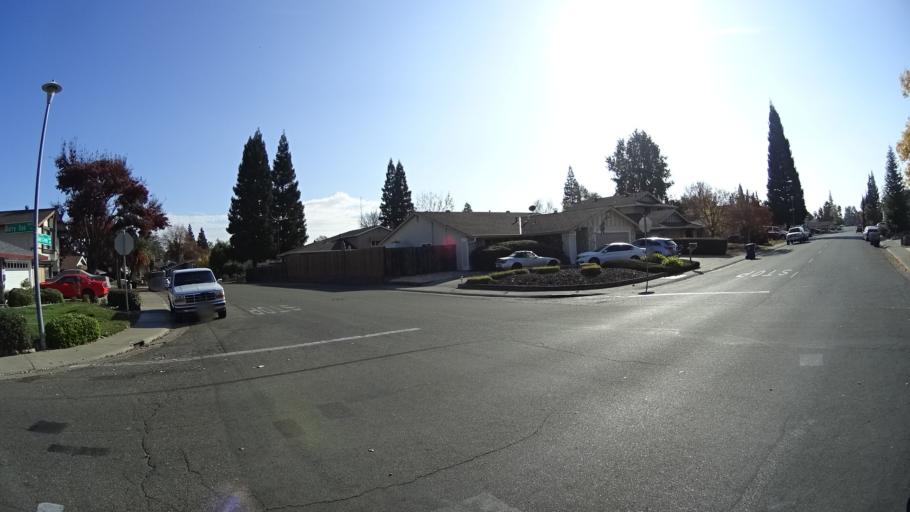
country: US
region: California
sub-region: Sacramento County
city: Citrus Heights
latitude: 38.7129
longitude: -121.2621
